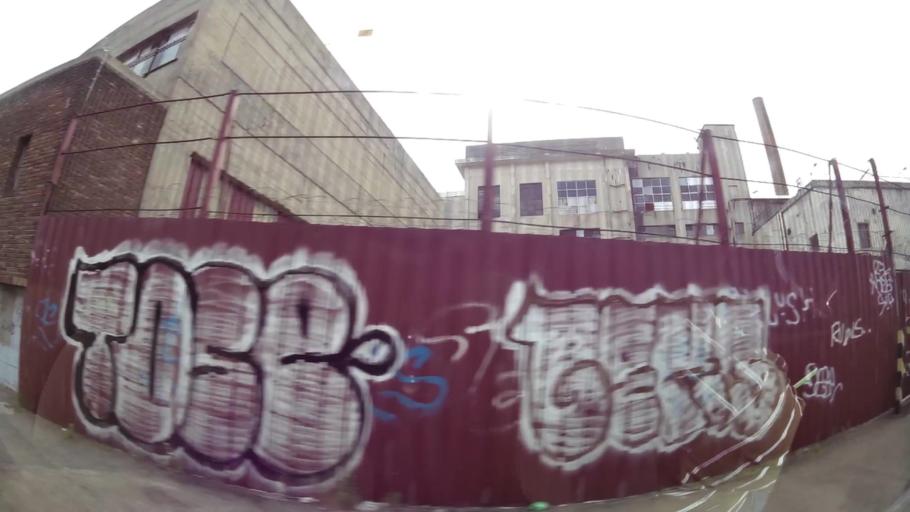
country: UY
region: Montevideo
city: Montevideo
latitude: -34.8820
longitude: -56.1983
